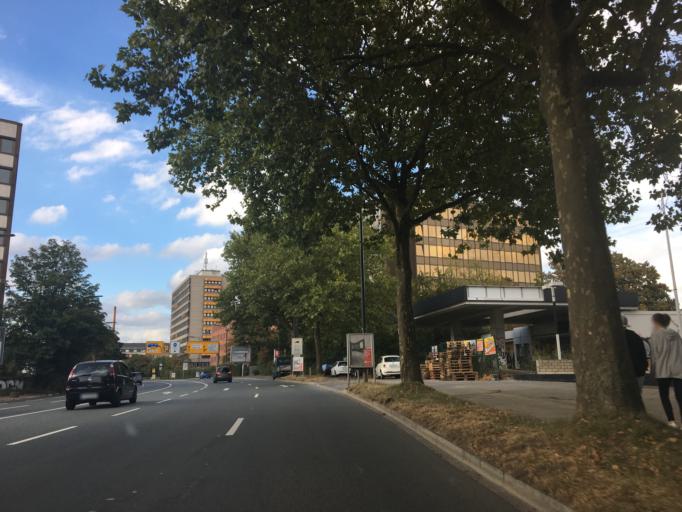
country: DE
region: North Rhine-Westphalia
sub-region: Regierungsbezirk Dusseldorf
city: Dusseldorf
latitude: 51.2016
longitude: 6.7874
